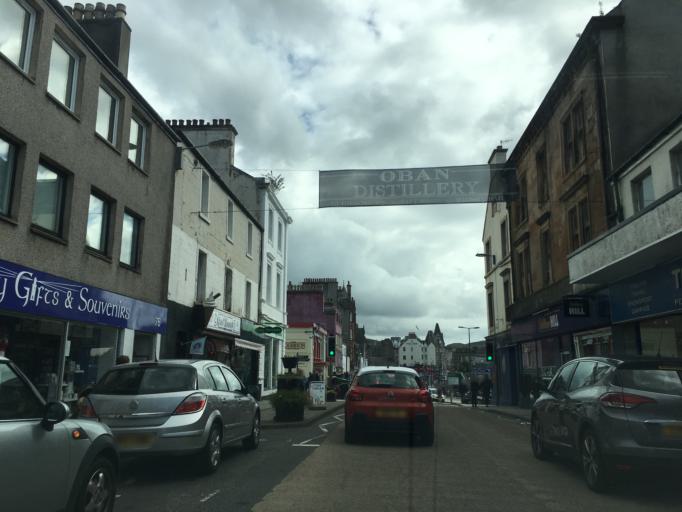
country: GB
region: Scotland
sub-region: Argyll and Bute
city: Oban
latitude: 56.4154
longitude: -5.4728
